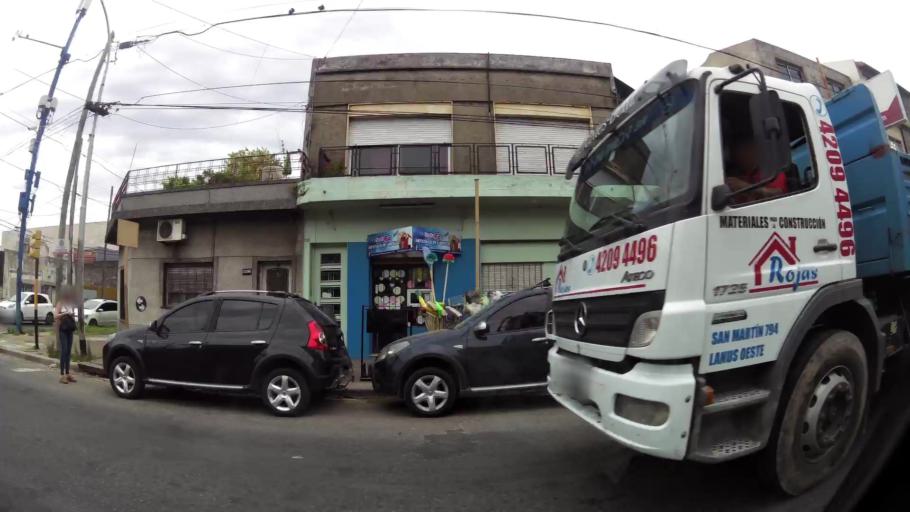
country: AR
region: Buenos Aires
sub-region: Partido de Lanus
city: Lanus
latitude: -34.6807
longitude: -58.3908
